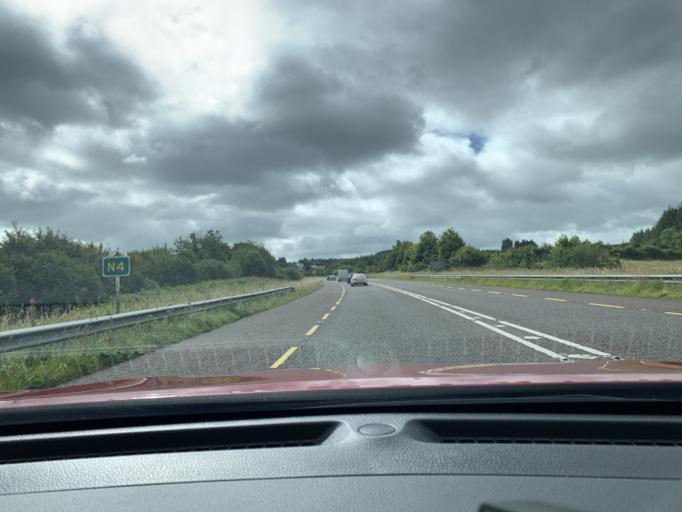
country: IE
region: Connaught
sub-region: Roscommon
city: Boyle
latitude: 54.0260
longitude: -8.3374
